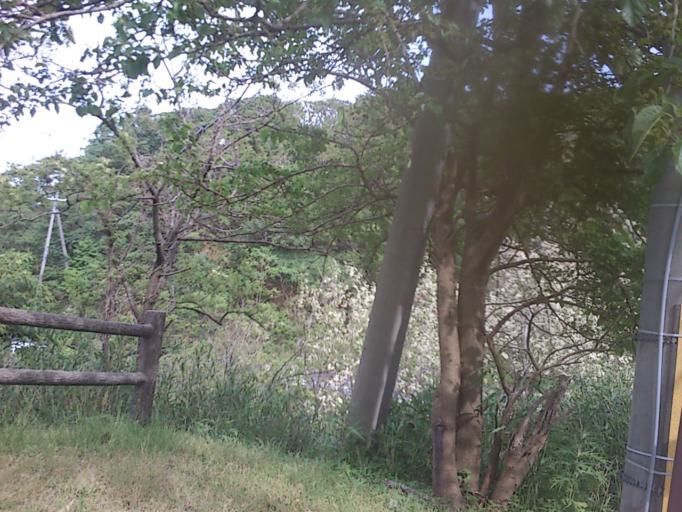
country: JP
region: Hyogo
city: Toyooka
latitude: 35.6922
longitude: 135.0036
